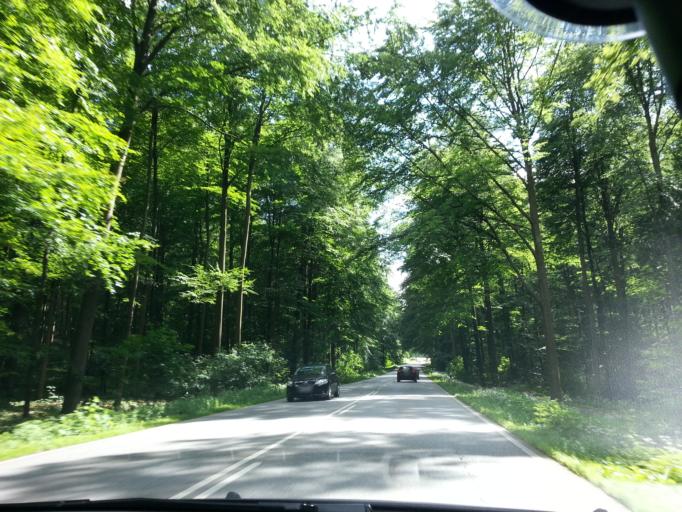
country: DE
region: Schleswig-Holstein
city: Fredeburg
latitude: 53.6563
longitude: 10.7135
